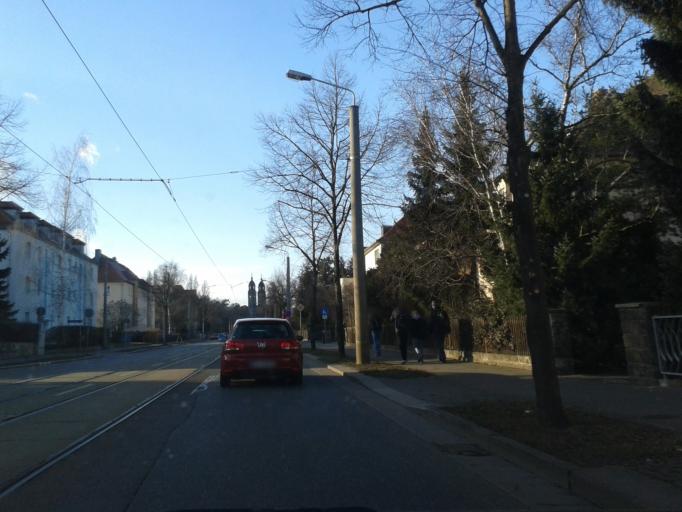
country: DE
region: Saxony
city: Dresden
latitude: 51.0226
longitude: 13.7746
